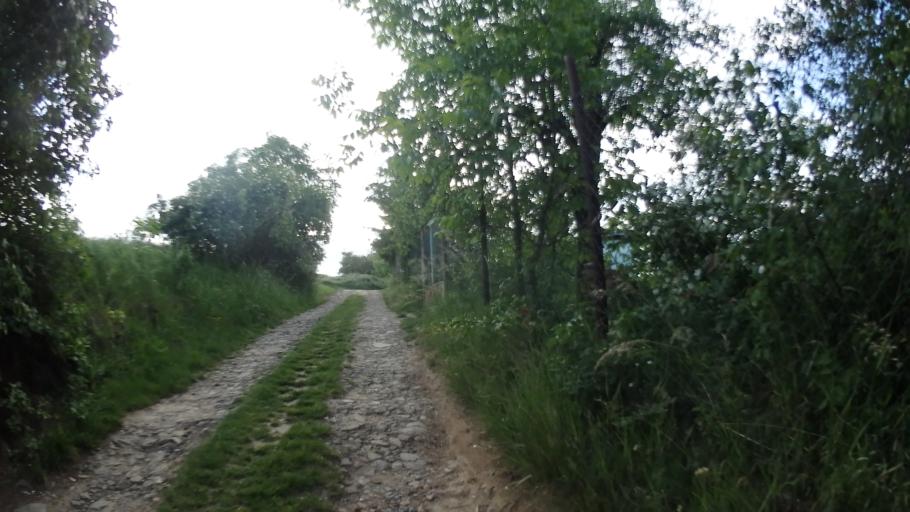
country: CZ
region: South Moravian
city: Moravany
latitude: 49.1593
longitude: 16.5887
